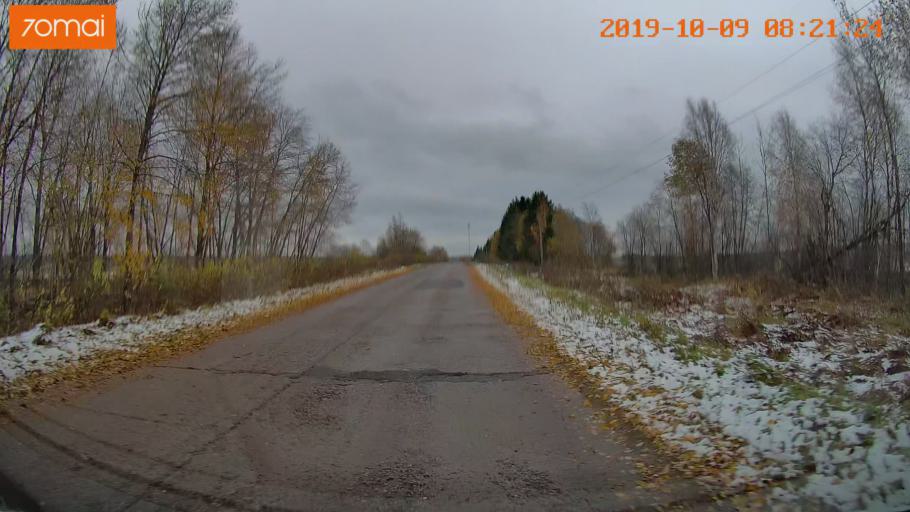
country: RU
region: Vologda
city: Gryazovets
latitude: 58.7421
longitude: 40.2762
